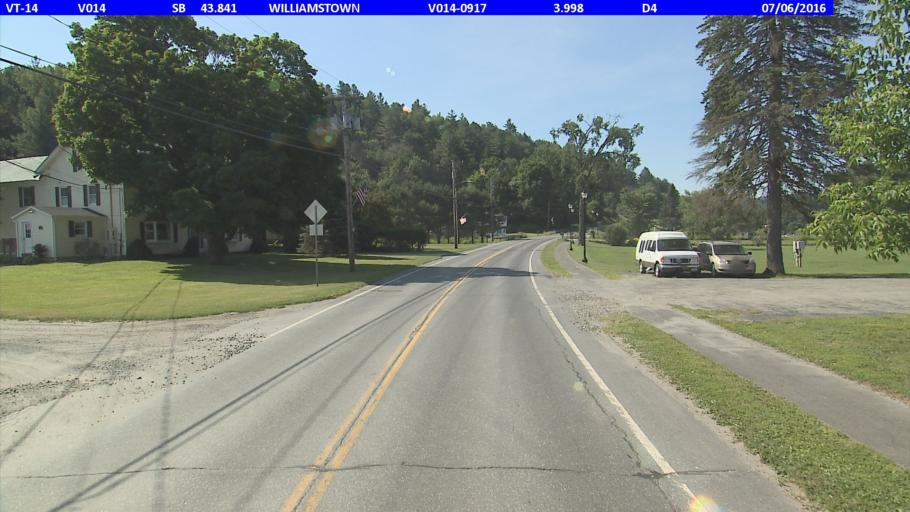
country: US
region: Vermont
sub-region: Orange County
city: Williamstown
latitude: 44.1155
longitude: -72.5397
